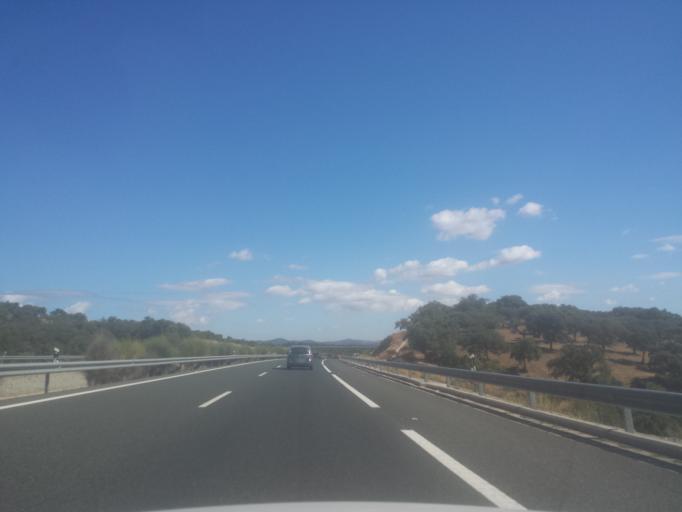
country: ES
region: Andalusia
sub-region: Provincia de Huelva
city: Santa Olalla del Cala
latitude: 37.9271
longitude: -6.2278
